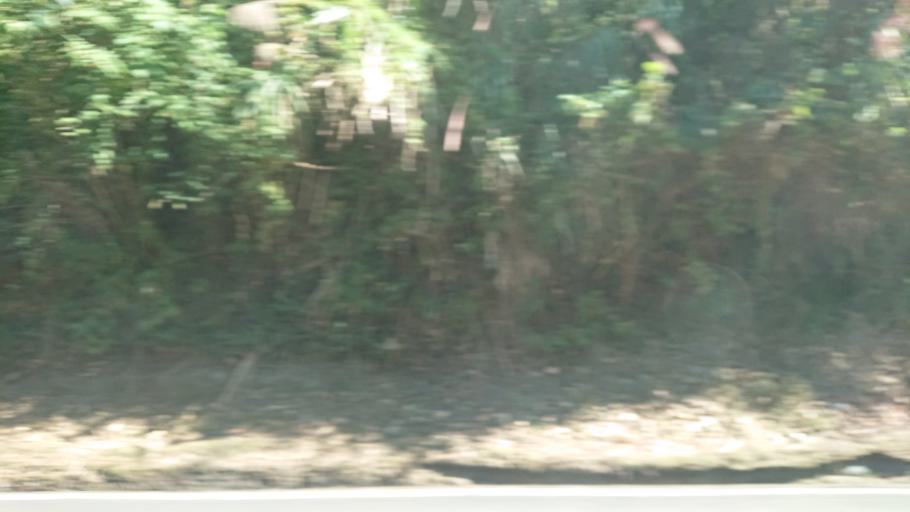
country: TW
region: Taiwan
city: Lugu
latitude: 23.4916
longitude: 120.7560
